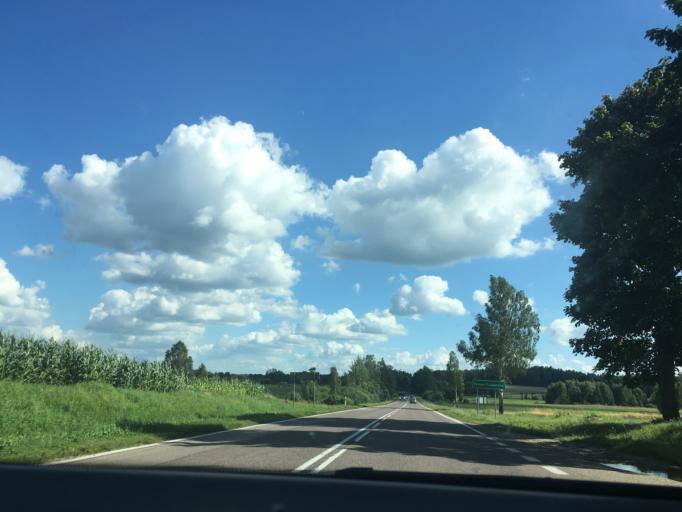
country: PL
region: Podlasie
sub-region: Powiat bialostocki
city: Dobrzyniewo Duze
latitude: 53.3441
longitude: 23.0994
